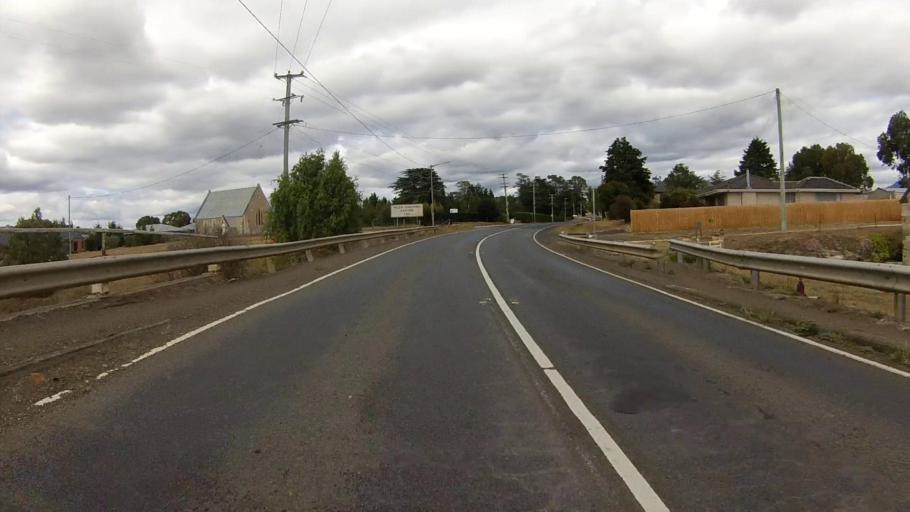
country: AU
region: Tasmania
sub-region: Brighton
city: Bridgewater
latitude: -42.6855
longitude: 147.2657
